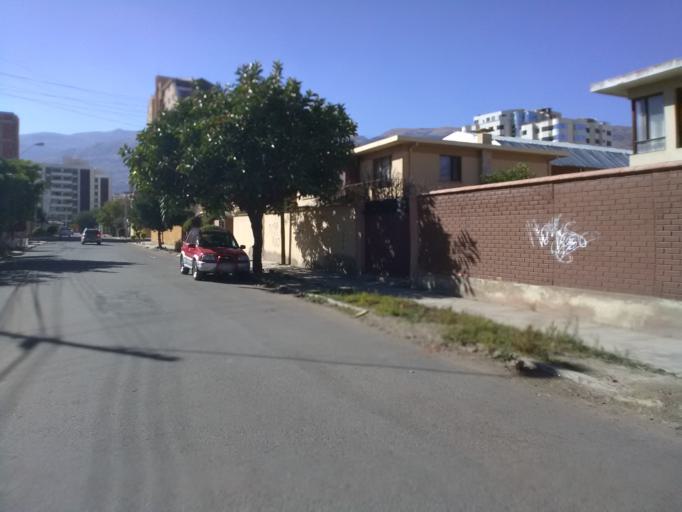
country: BO
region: Cochabamba
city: Cochabamba
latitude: -17.3741
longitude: -66.1643
